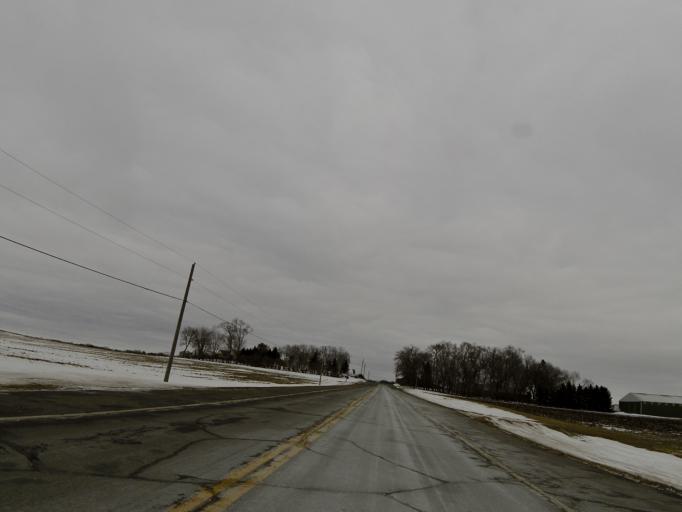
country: US
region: Minnesota
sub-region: Washington County
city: Cottage Grove
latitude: 44.8335
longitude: -92.8974
